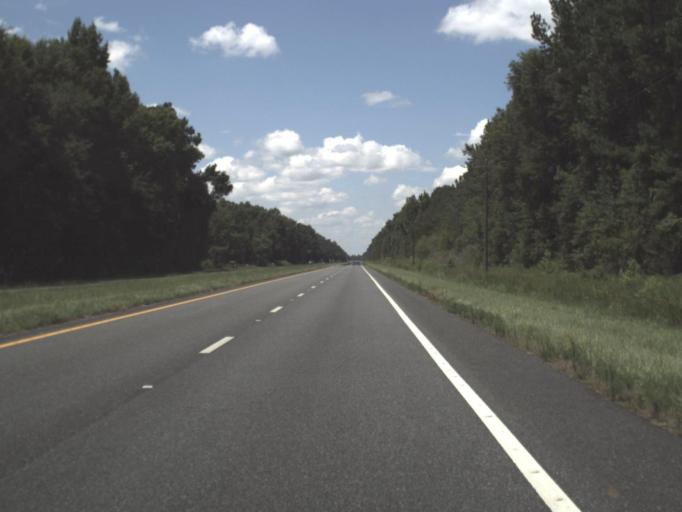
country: US
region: Florida
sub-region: Taylor County
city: Perry
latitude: 30.2934
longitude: -83.7390
